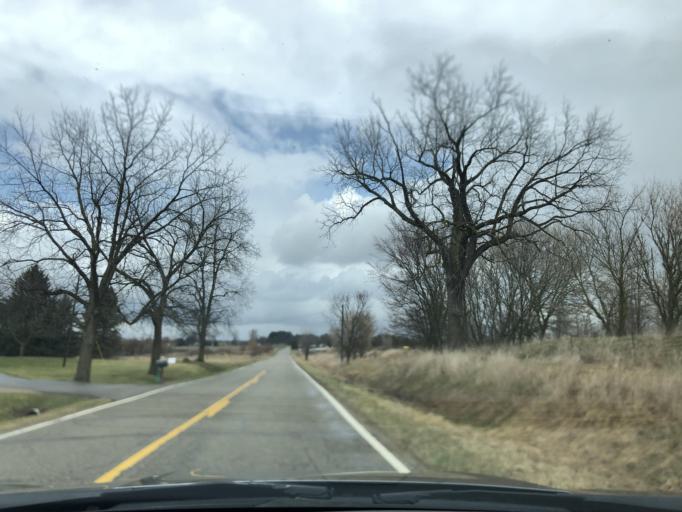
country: US
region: Michigan
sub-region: Clinton County
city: Saint Johns
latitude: 43.0515
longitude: -84.6013
